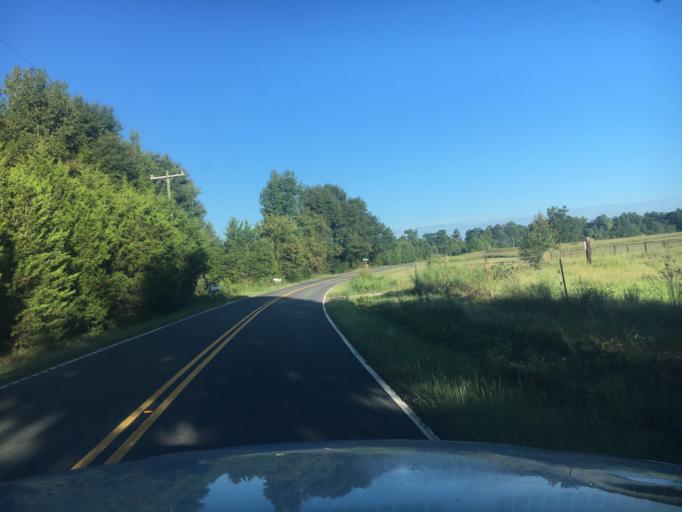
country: US
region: South Carolina
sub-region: Spartanburg County
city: Woodruff
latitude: 34.6348
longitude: -82.0084
